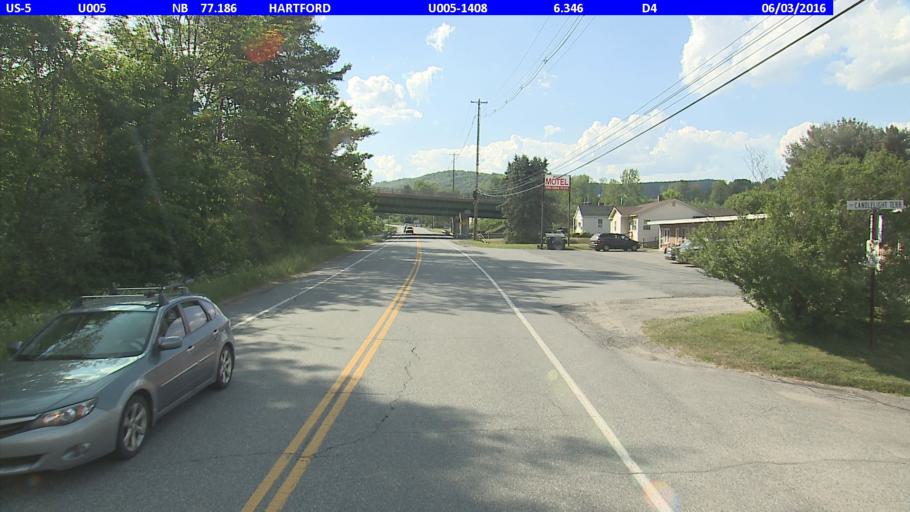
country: US
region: Vermont
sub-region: Windsor County
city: Wilder
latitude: 43.6816
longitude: -72.3140
